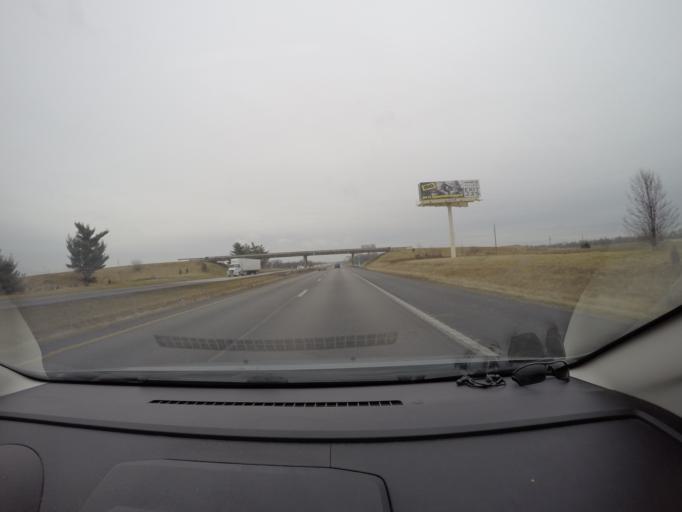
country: US
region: Missouri
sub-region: Gasconade County
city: Hermann
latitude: 38.8661
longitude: -91.3318
